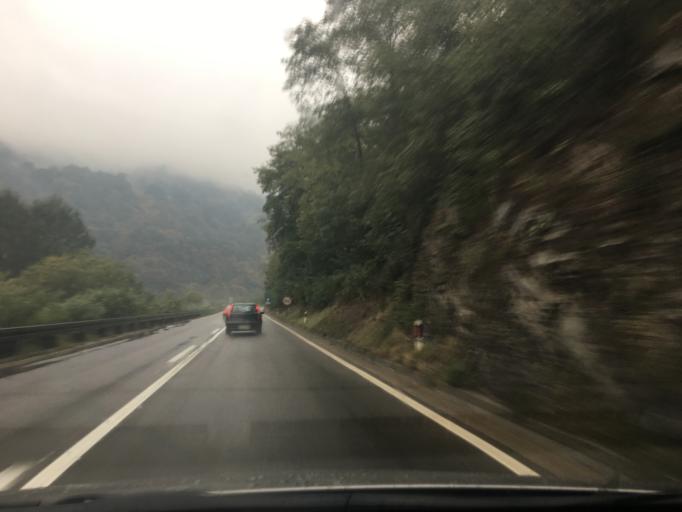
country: RS
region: Central Serbia
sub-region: Pcinjski Okrug
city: Vladicin Han
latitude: 42.7339
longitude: 22.0620
